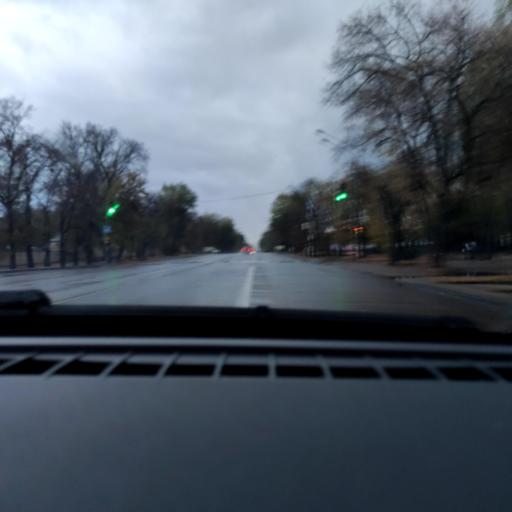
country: RU
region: Voronezj
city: Voronezh
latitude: 51.6574
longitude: 39.2752
